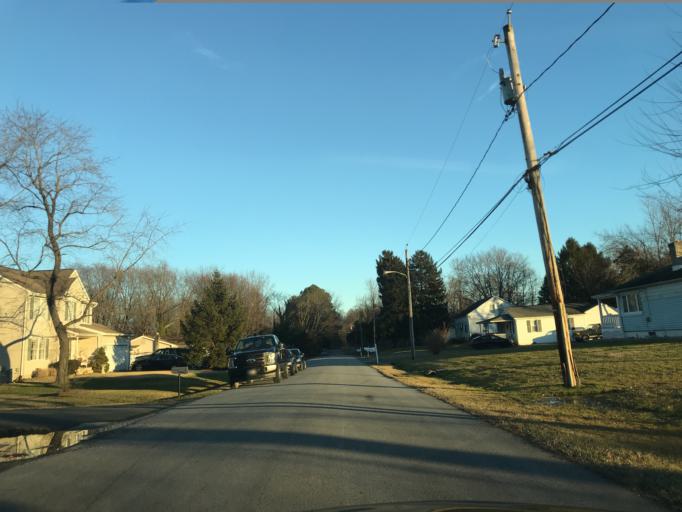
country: US
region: Maryland
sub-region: Baltimore County
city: Bowleys Quarters
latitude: 39.3715
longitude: -76.3485
